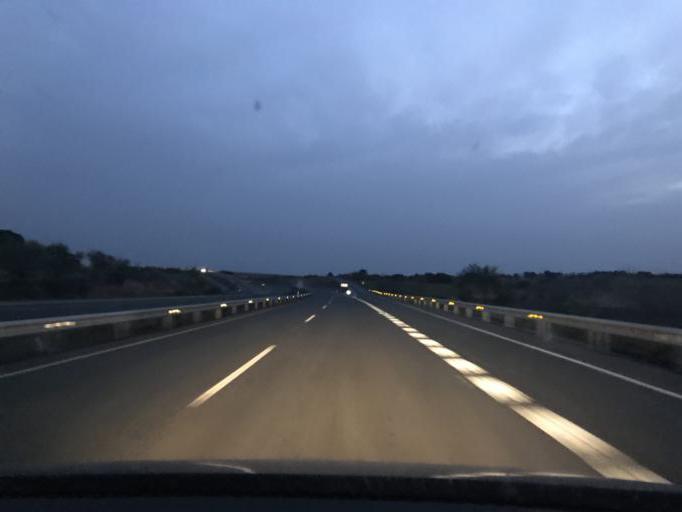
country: ES
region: Andalusia
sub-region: Provincia de Granada
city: Gor
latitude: 37.4006
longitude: -2.9435
